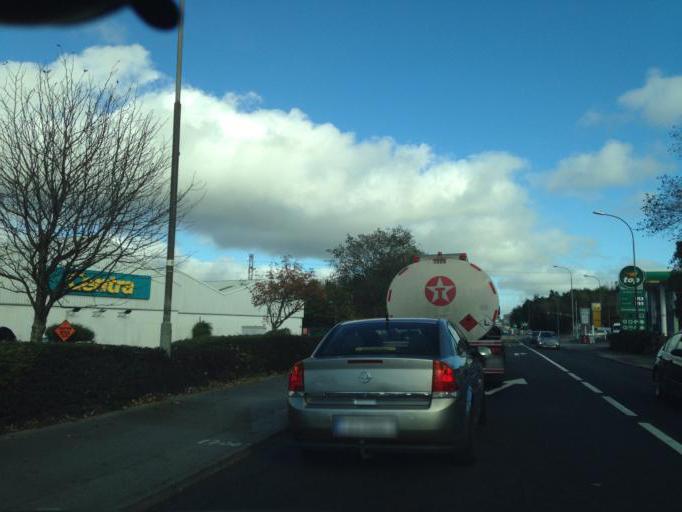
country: IE
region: Connaught
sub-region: County Galway
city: Gaillimh
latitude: 53.2897
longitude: -9.0218
